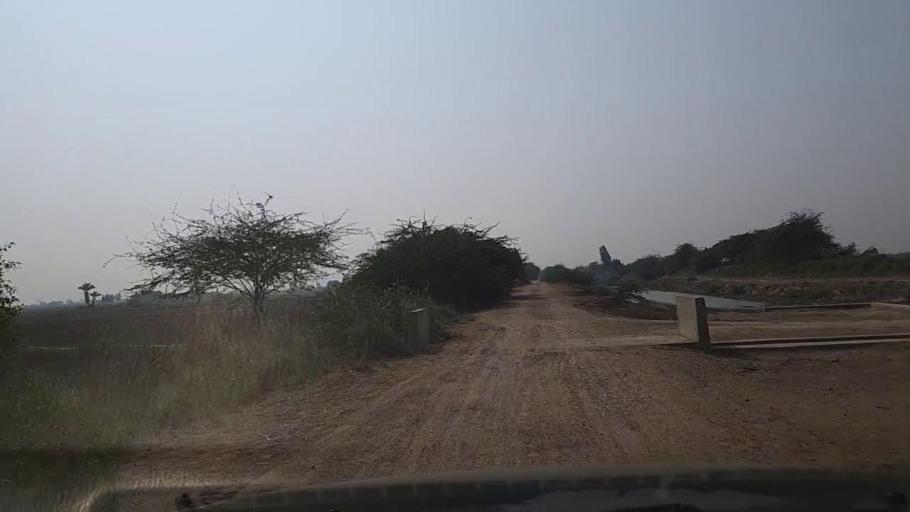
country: PK
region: Sindh
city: Thatta
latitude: 24.7779
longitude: 67.8344
